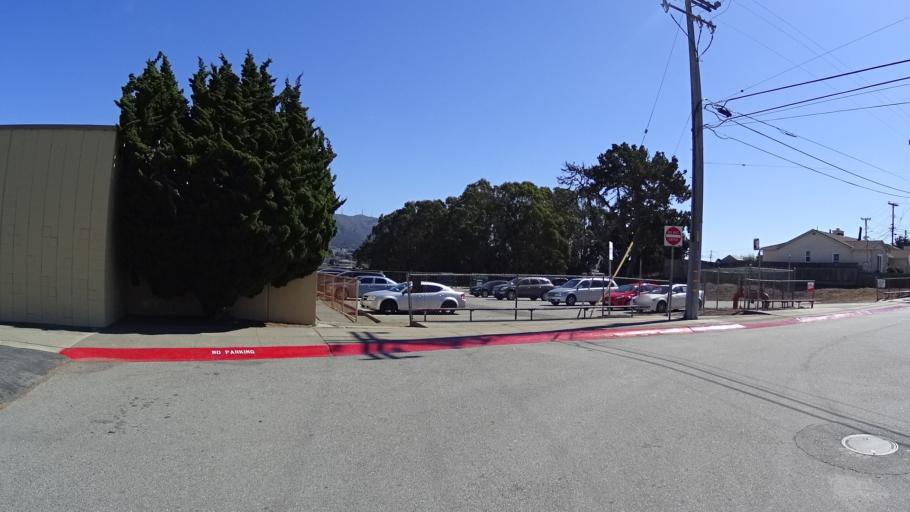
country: US
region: California
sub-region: San Mateo County
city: Broadmoor
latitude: 37.6947
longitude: -122.4822
